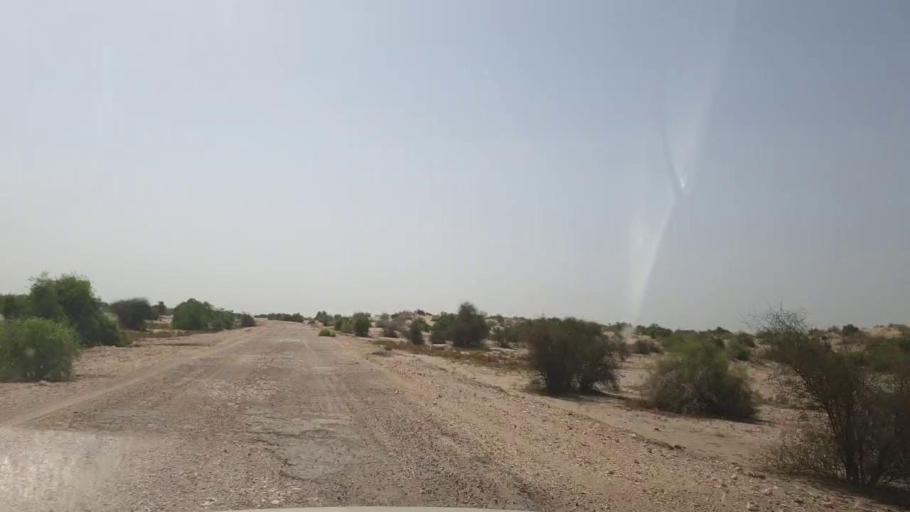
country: PK
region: Sindh
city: Rohri
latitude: 27.4362
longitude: 69.2462
